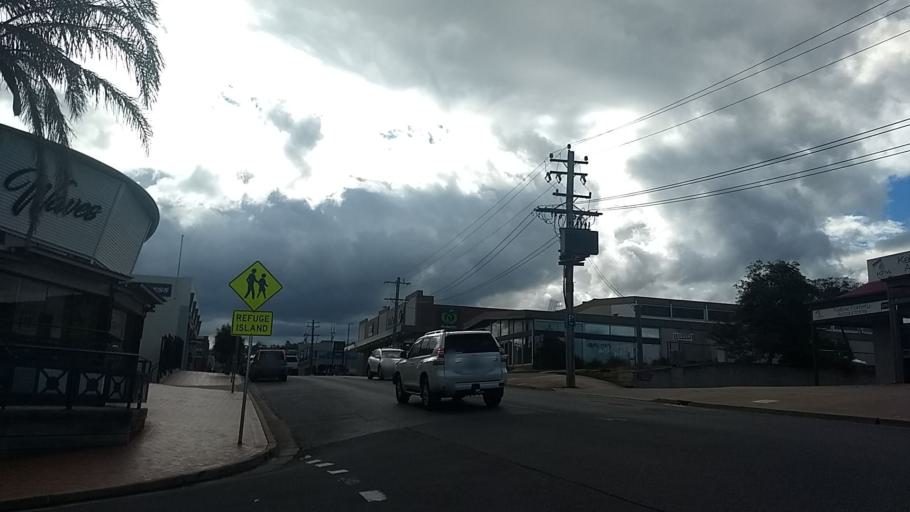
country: AU
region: New South Wales
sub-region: Bega Valley
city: Merimbula
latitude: -36.8869
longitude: 149.9106
